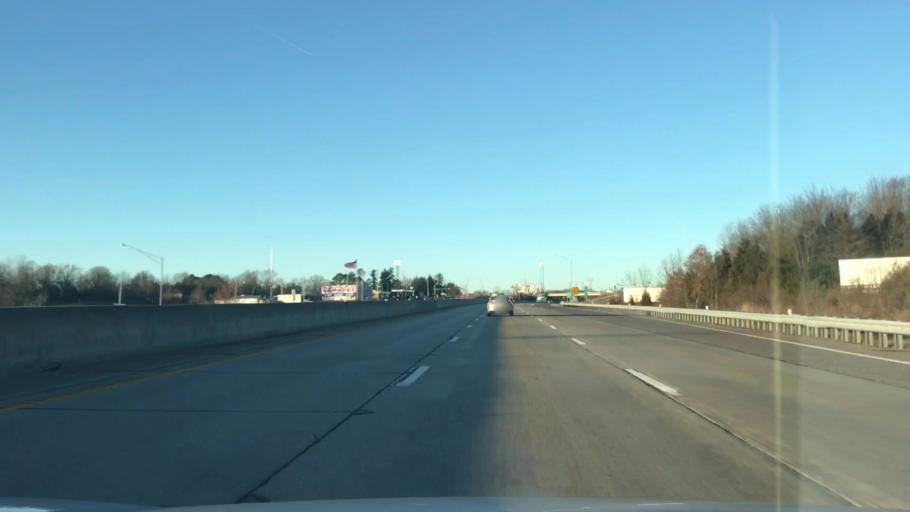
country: US
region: Missouri
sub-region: Franklin County
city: Gray Summit
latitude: 38.4850
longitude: -90.8166
